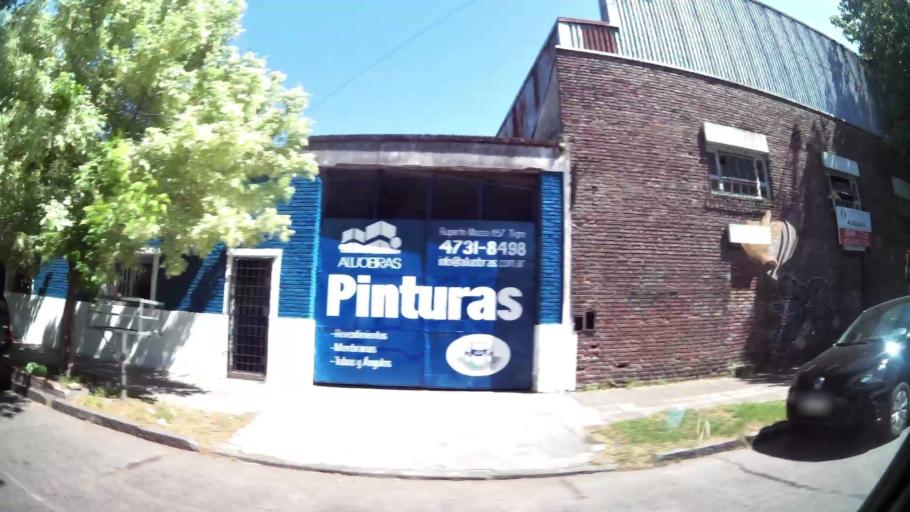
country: AR
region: Buenos Aires
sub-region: Partido de Tigre
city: Tigre
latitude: -34.4349
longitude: -58.5690
